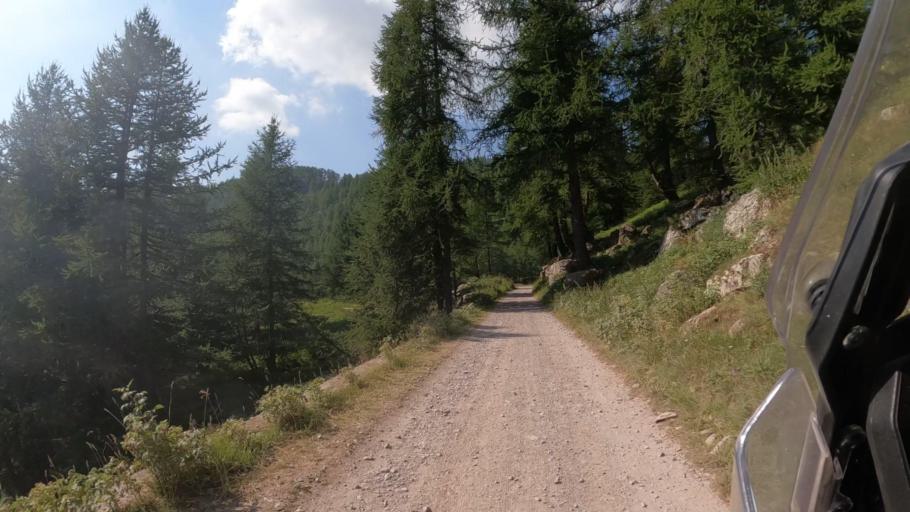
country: IT
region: Piedmont
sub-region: Provincia di Cuneo
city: Briga Alta
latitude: 44.1042
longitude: 7.7096
